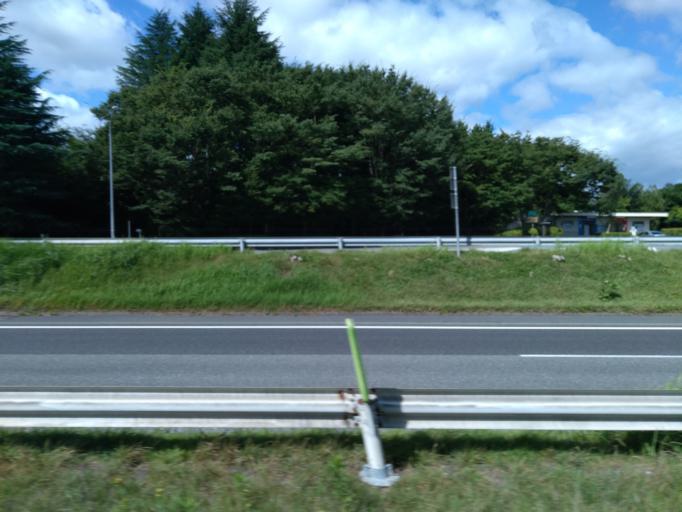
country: JP
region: Iwate
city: Ichinoseki
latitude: 38.7470
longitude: 141.0468
